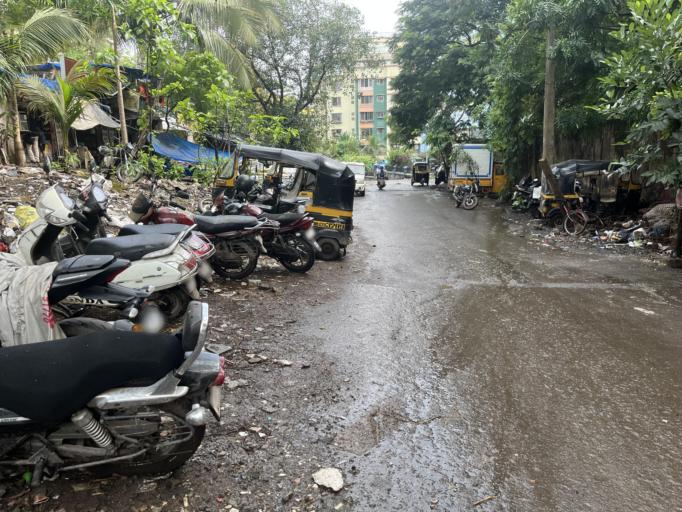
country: IN
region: Maharashtra
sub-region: Mumbai Suburban
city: Borivli
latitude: 19.2265
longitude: 72.8660
